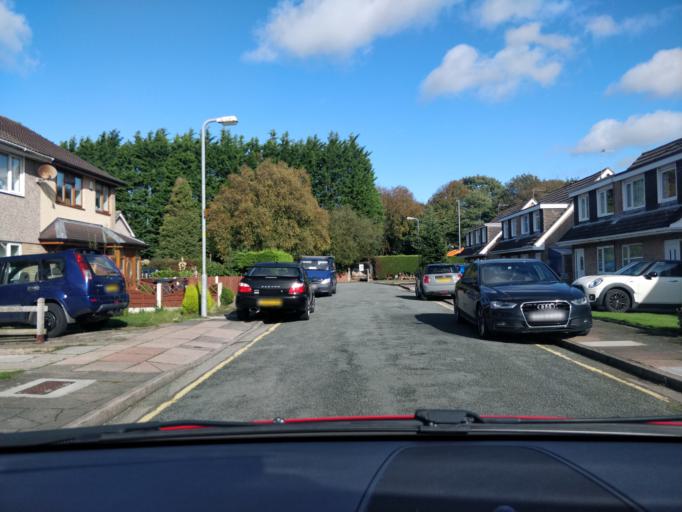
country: GB
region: England
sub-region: Sefton
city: Southport
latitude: 53.6325
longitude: -2.9742
